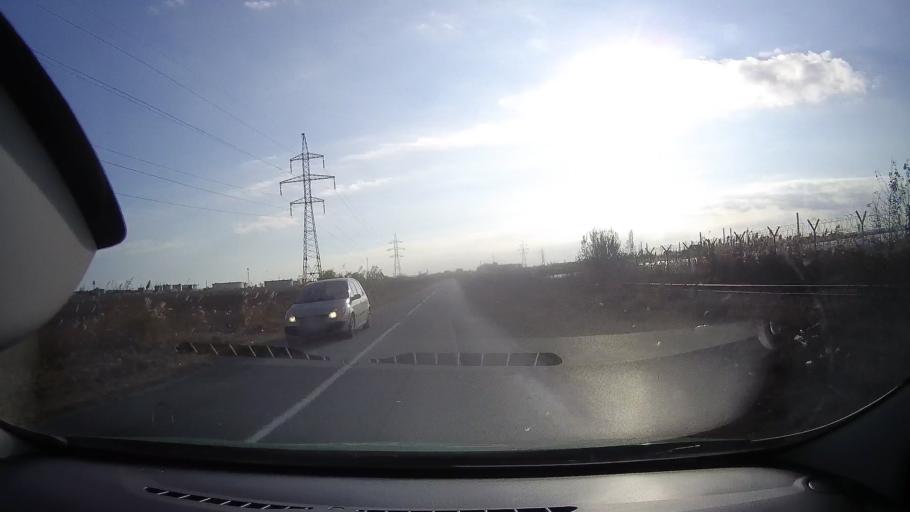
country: RO
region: Constanta
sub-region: Comuna Corbu
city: Corbu
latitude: 44.3593
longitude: 28.6759
